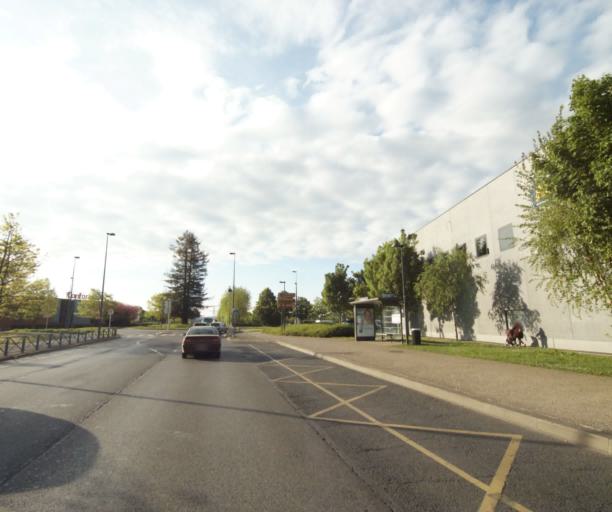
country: FR
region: Ile-de-France
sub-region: Departement de Seine-et-Marne
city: Torcy
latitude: 48.8431
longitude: 2.6552
